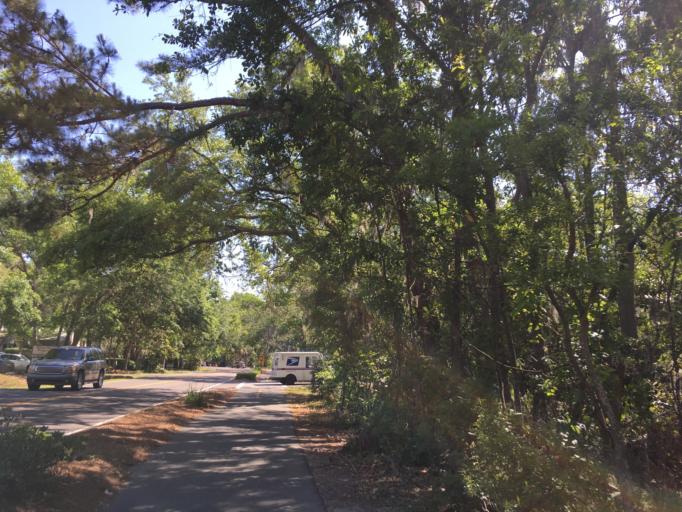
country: US
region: South Carolina
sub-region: Beaufort County
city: Hilton Head Island
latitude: 32.1576
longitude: -80.7543
